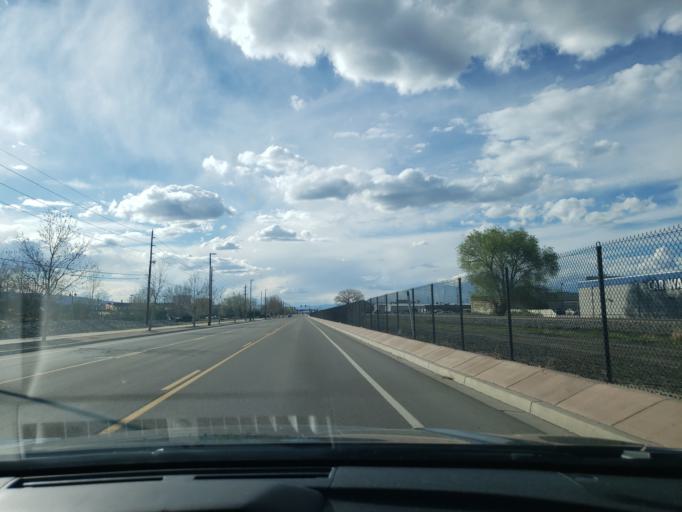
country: US
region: Colorado
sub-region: Mesa County
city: Redlands
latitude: 39.0834
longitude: -108.5943
